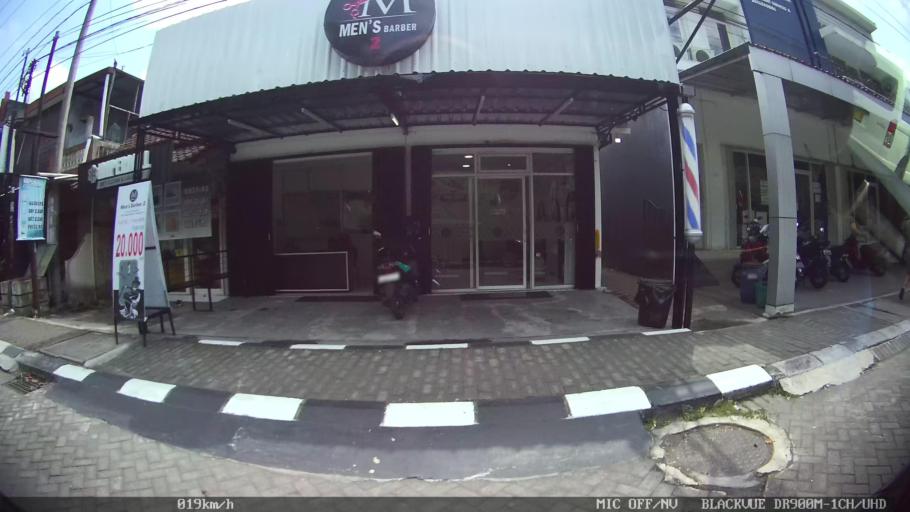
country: ID
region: Daerah Istimewa Yogyakarta
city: Yogyakarta
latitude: -7.7661
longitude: 110.3800
